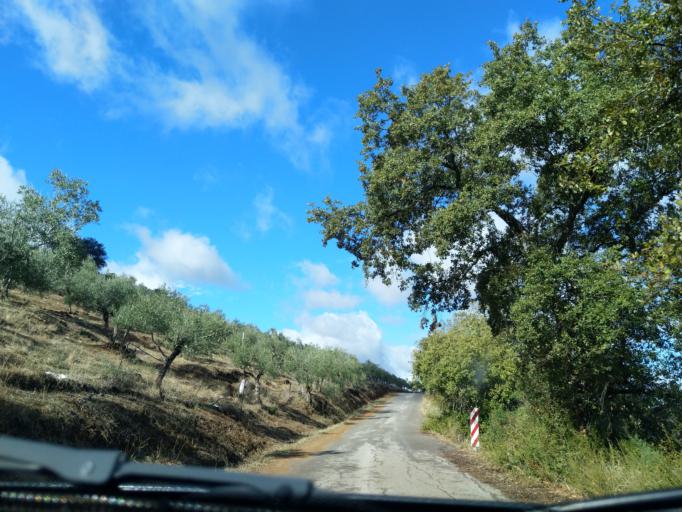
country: ES
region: Extremadura
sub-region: Provincia de Badajoz
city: Reina
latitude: 38.1271
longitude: -5.9211
